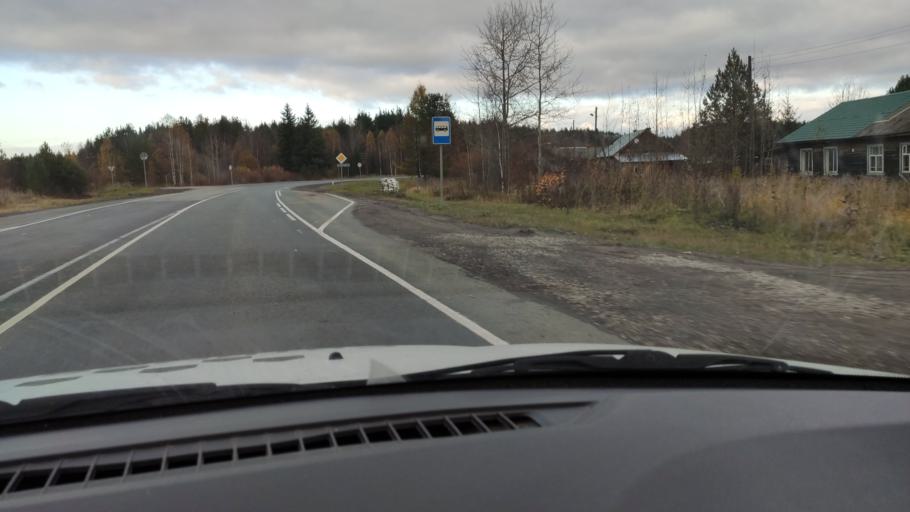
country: RU
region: Kirov
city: Belaya Kholunitsa
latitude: 58.8688
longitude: 50.8435
